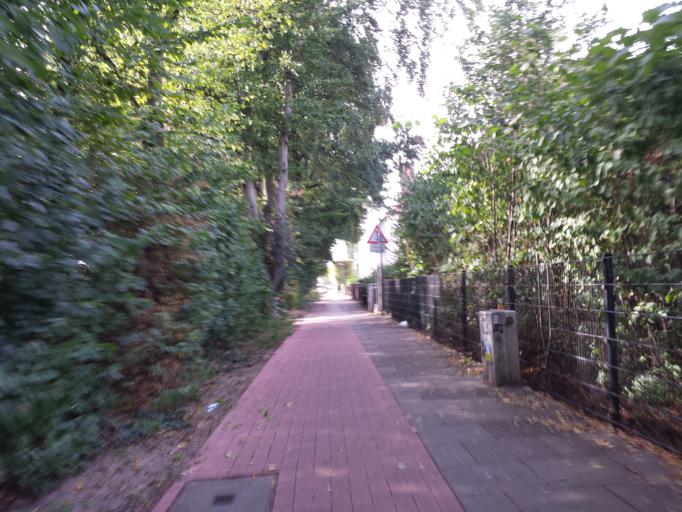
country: DE
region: Bremen
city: Bremen
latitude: 53.0617
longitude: 8.7899
